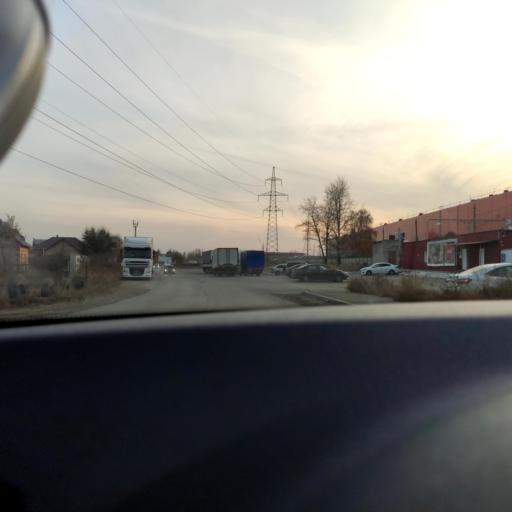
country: RU
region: Samara
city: Petra-Dubrava
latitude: 53.2575
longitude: 50.3126
